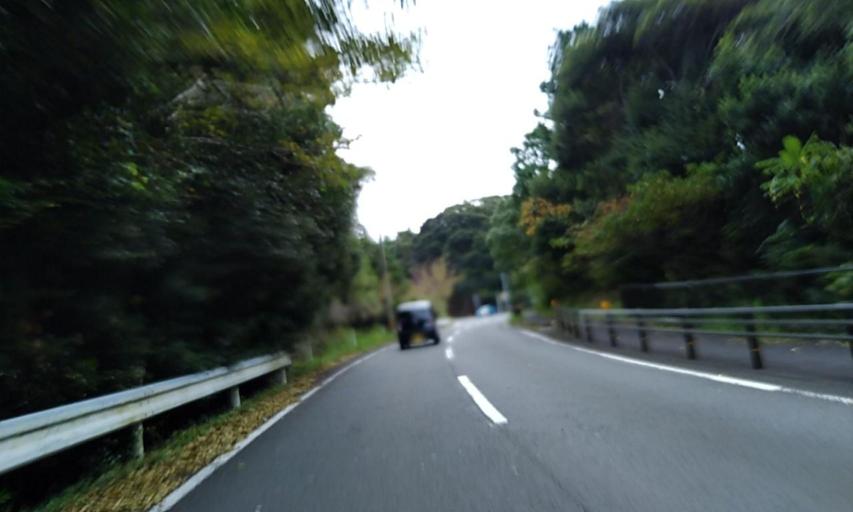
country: JP
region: Wakayama
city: Shingu
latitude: 33.4667
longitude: 135.8278
